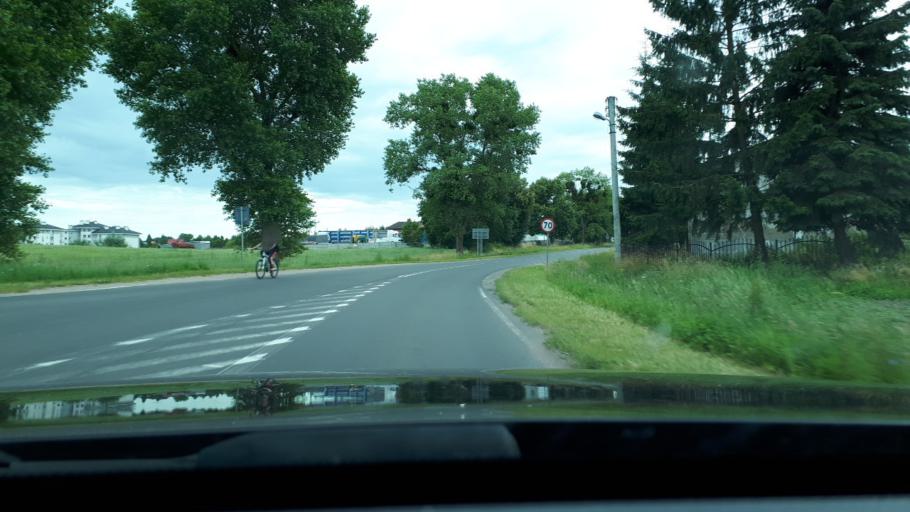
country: PL
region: Warmian-Masurian Voivodeship
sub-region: Powiat olsztynski
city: Olsztynek
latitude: 53.5778
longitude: 20.2780
